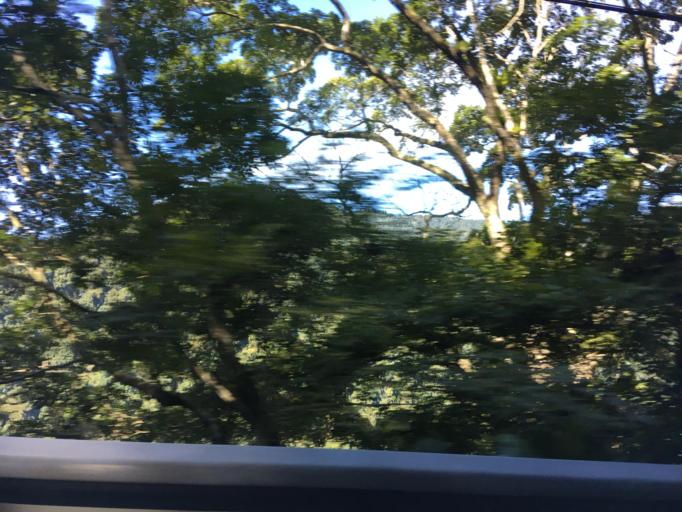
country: TW
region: Taiwan
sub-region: Yilan
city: Yilan
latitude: 24.5549
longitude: 121.5071
